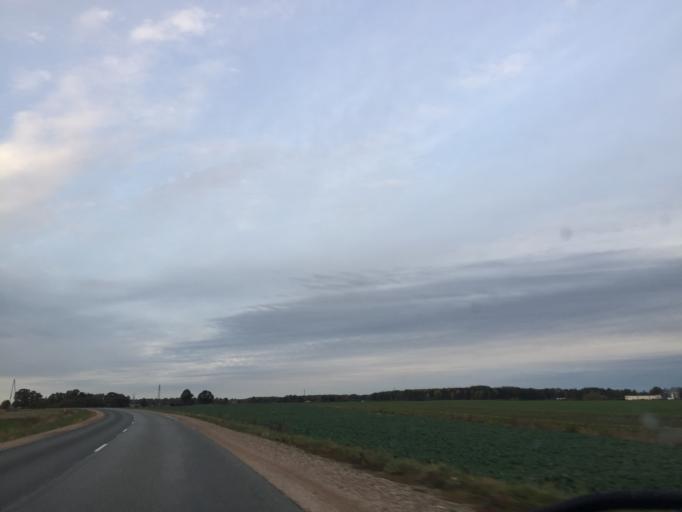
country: LV
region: Dobeles Rajons
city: Dobele
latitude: 56.7065
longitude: 23.3807
